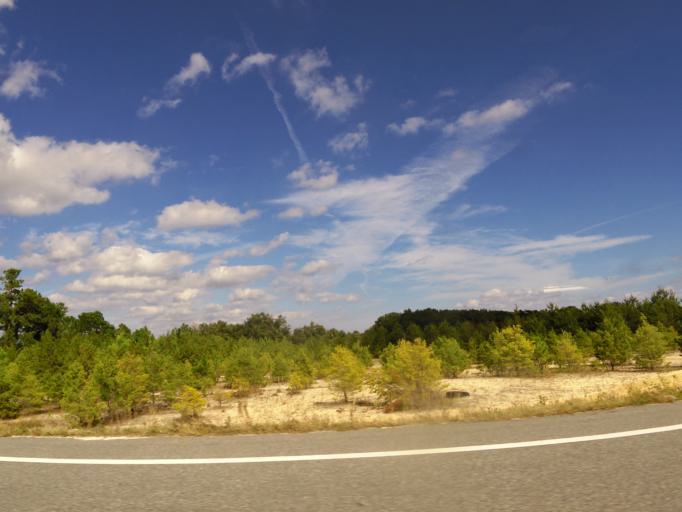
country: US
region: Florida
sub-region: Duval County
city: Jacksonville
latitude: 30.4148
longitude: -81.6275
